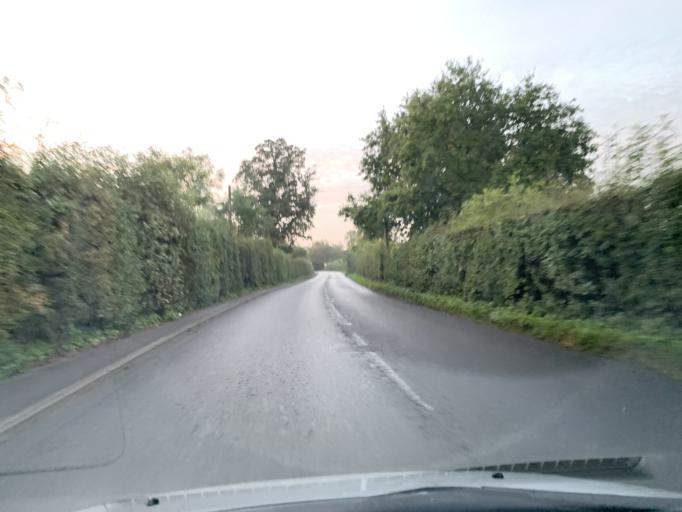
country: GB
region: England
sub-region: Wiltshire
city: Alderbury
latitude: 51.0480
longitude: -1.7450
